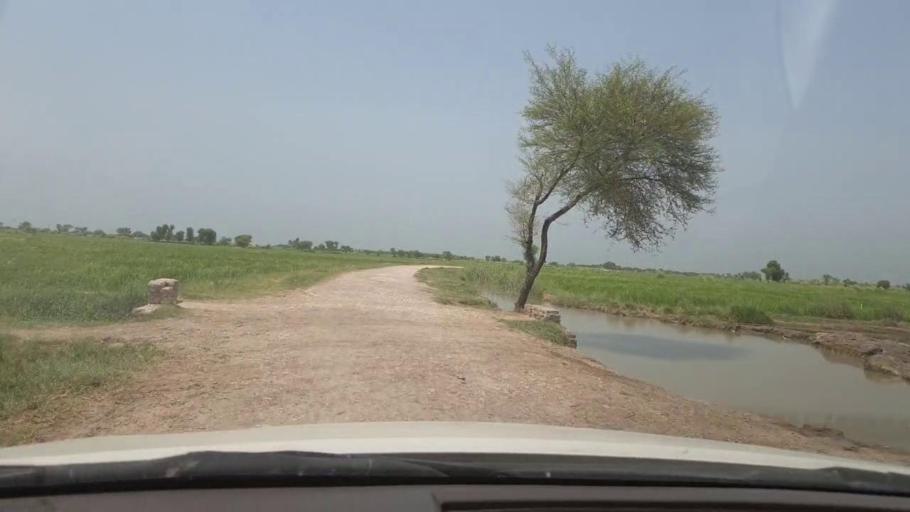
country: PK
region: Sindh
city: Shikarpur
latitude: 28.0734
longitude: 68.5743
